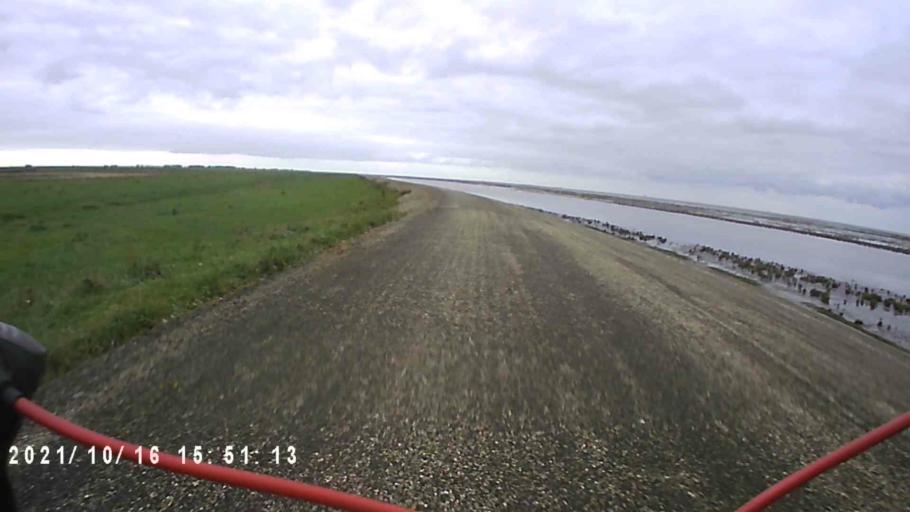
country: NL
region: Friesland
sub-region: Gemeente Dongeradeel
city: Anjum
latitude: 53.4043
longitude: 6.1337
